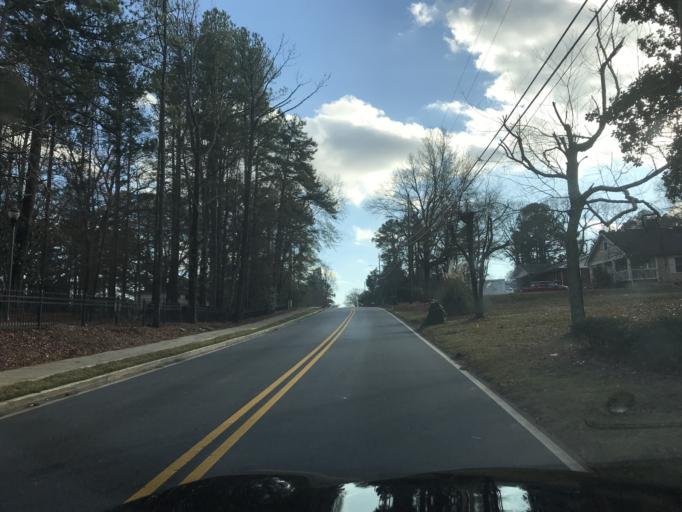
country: US
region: Georgia
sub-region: Fulton County
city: College Park
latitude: 33.6338
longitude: -84.4726
